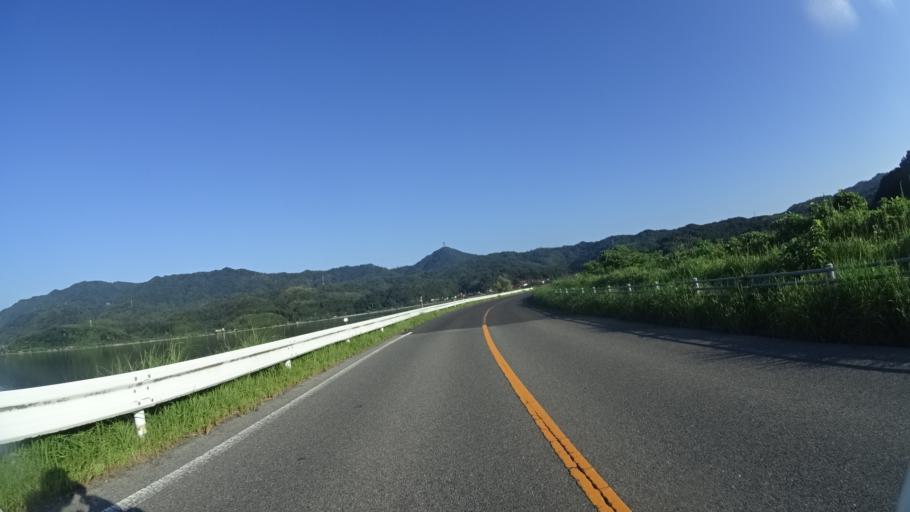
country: JP
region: Shimane
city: Sakaiminato
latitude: 35.5325
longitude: 133.1614
